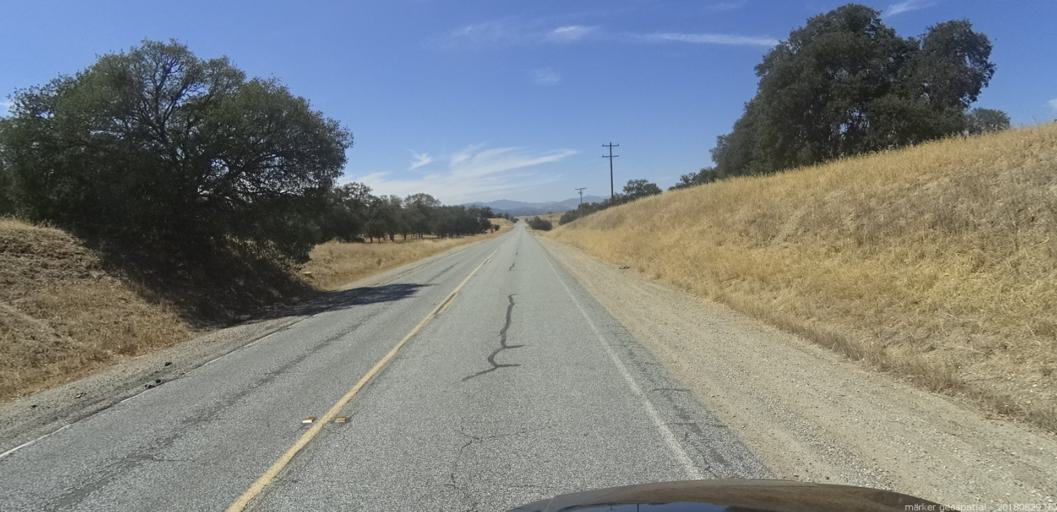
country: US
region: California
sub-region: Monterey County
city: King City
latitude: 35.9385
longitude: -121.1115
